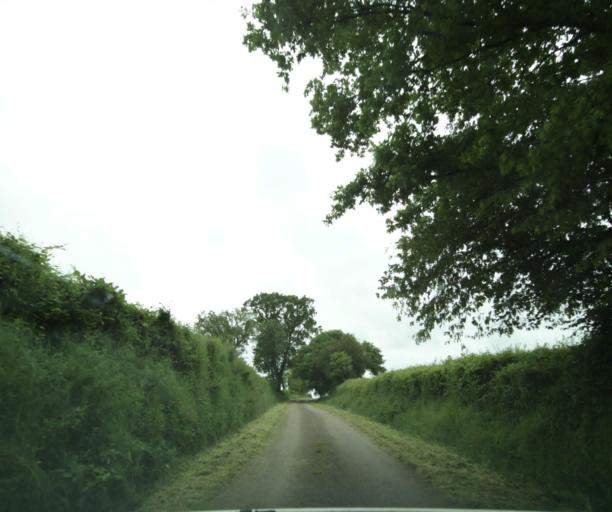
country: FR
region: Bourgogne
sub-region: Departement de Saone-et-Loire
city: Charolles
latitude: 46.4707
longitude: 4.2990
